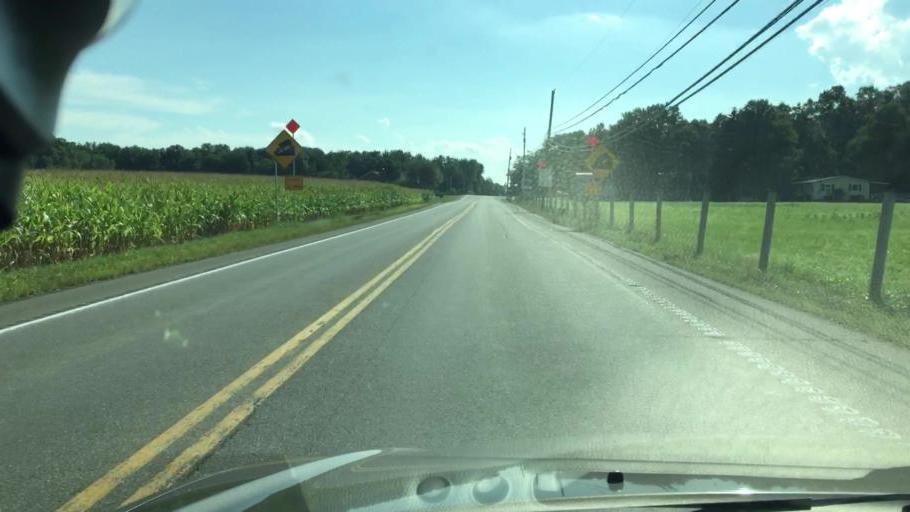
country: US
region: Pennsylvania
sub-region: Carbon County
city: Jim Thorpe
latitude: 40.8960
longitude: -75.6895
